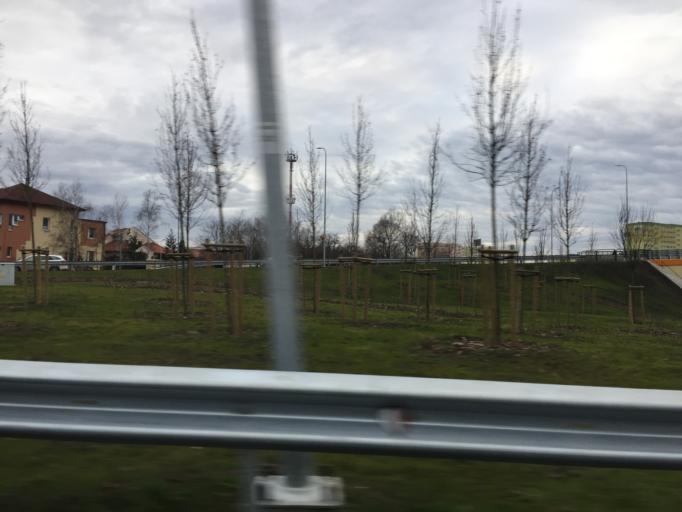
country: PL
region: Kujawsko-Pomorskie
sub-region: Bydgoszcz
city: Bydgoszcz
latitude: 53.1101
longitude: 18.0180
